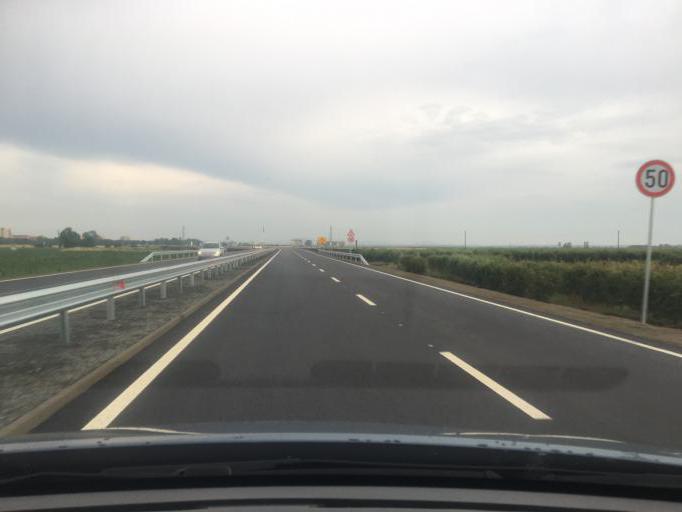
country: BG
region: Burgas
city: Aheloy
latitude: 42.6488
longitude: 27.6369
